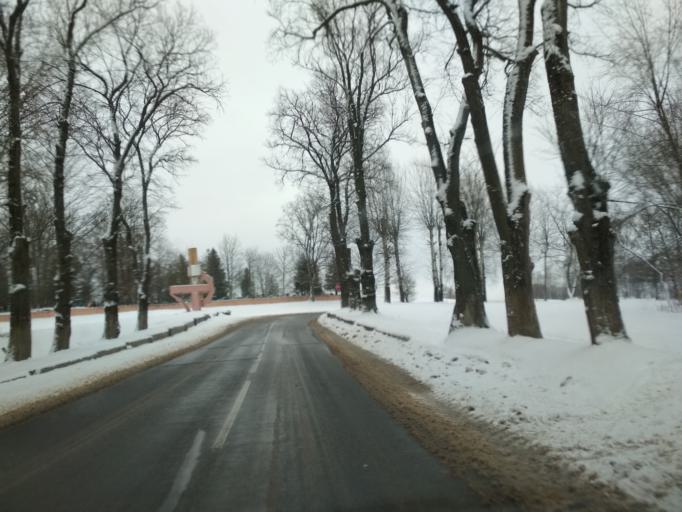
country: BY
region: Minsk
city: Mar''ina Horka
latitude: 53.5298
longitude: 28.1289
